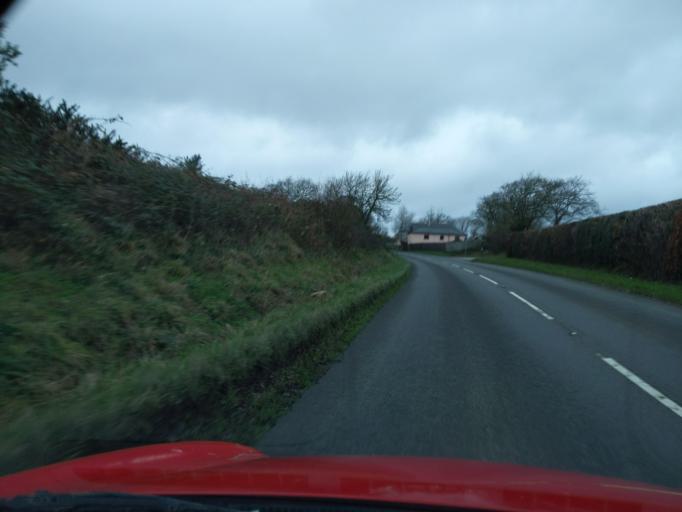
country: GB
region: England
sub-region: Devon
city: Holsworthy
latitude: 50.7758
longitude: -4.3348
